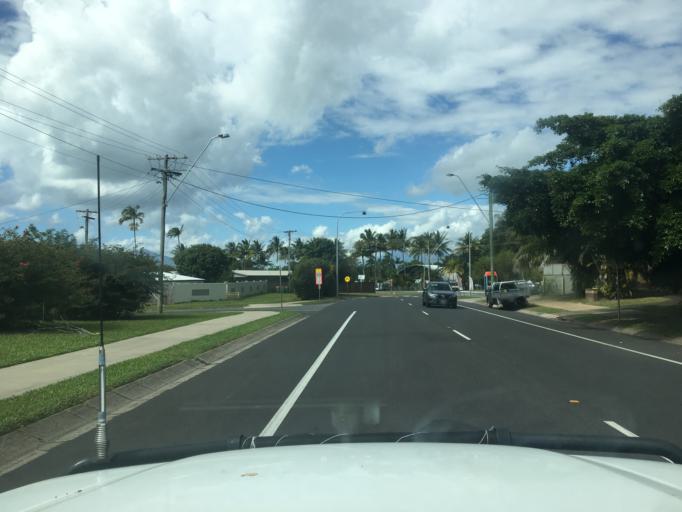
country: AU
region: Queensland
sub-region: Cairns
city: Woree
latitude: -16.9663
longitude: 145.7412
